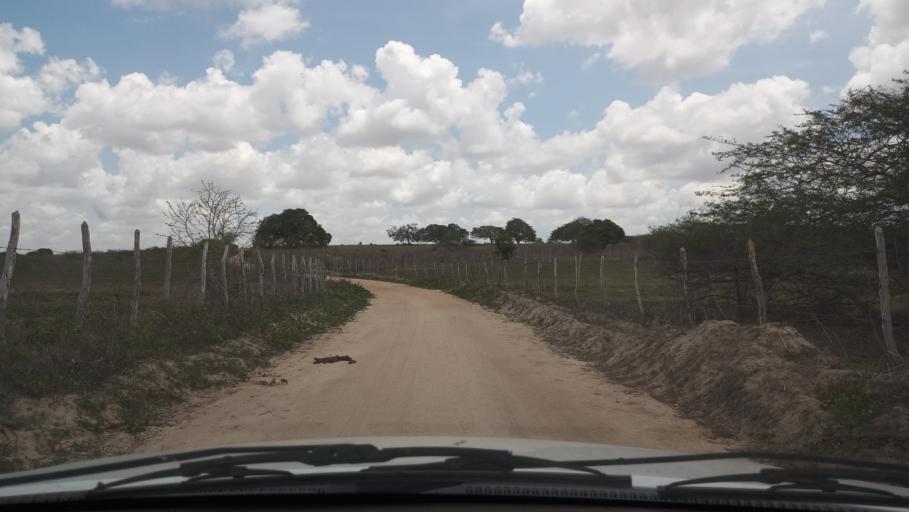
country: BR
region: Rio Grande do Norte
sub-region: Brejinho
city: Brejinho
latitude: -6.2968
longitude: -35.3525
